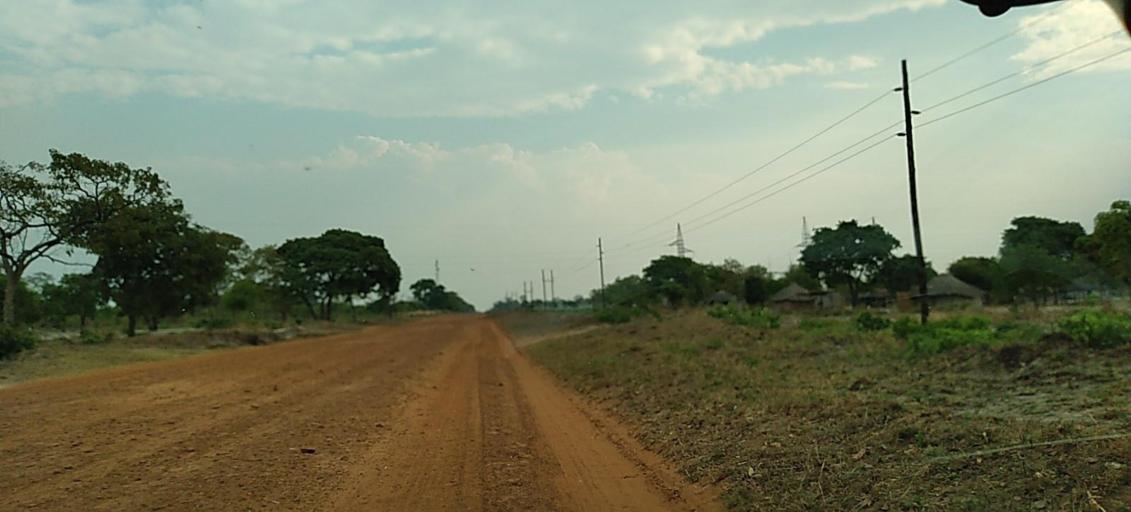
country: ZM
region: North-Western
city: Kabompo
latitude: -13.8760
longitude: 23.6658
